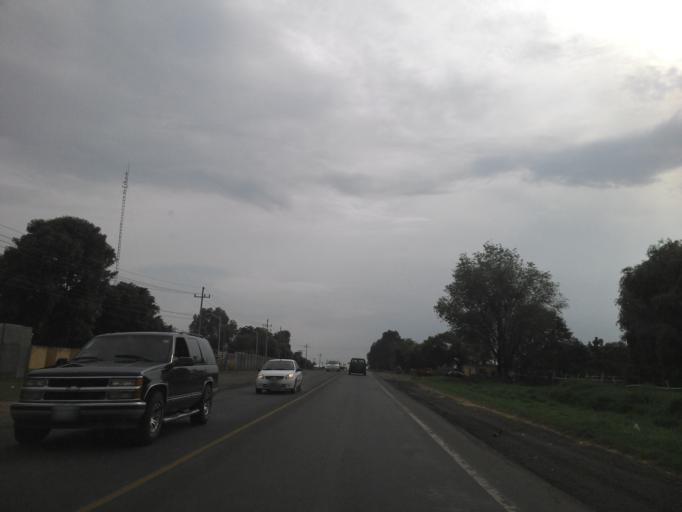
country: MX
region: Jalisco
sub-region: Acatic
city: Tierras Coloradas
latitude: 20.7580
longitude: -102.8231
